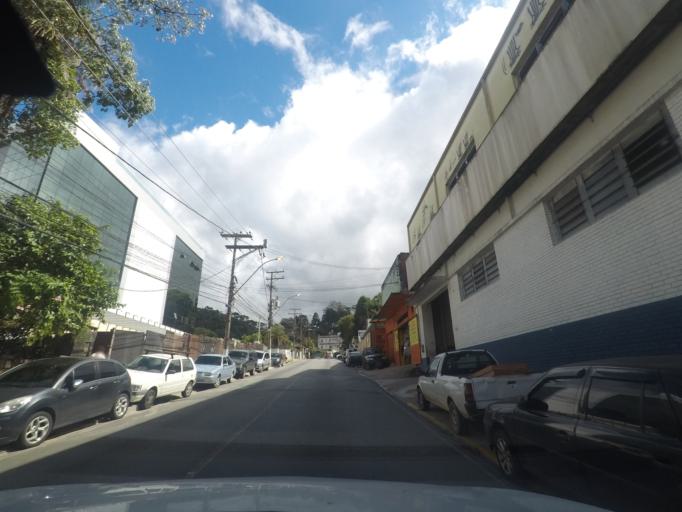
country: BR
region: Rio de Janeiro
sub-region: Teresopolis
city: Teresopolis
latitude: -22.3993
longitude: -42.9609
